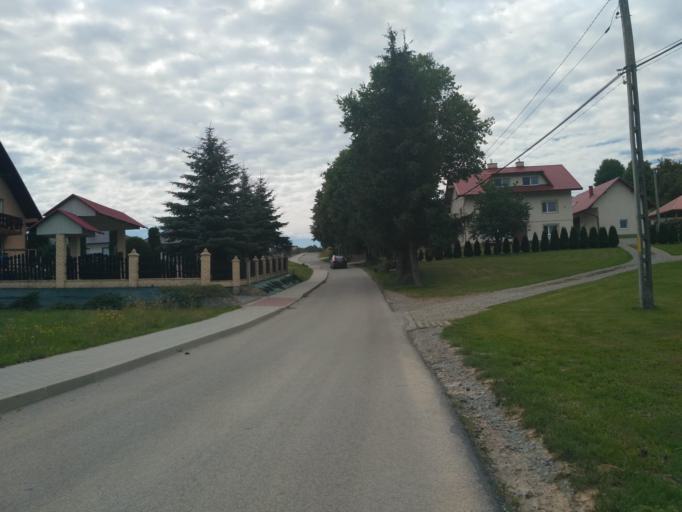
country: PL
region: Subcarpathian Voivodeship
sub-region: Powiat rzeszowski
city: Straszydle
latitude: 49.8989
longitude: 21.9805
